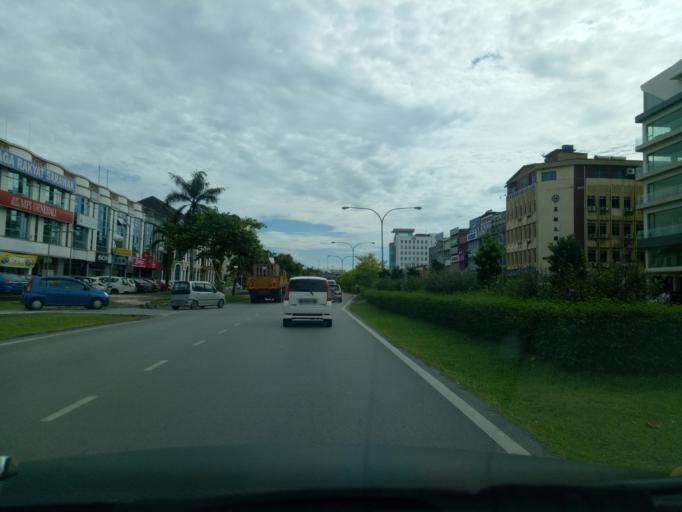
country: MY
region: Sarawak
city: Kuching
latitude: 1.5509
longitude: 110.3377
